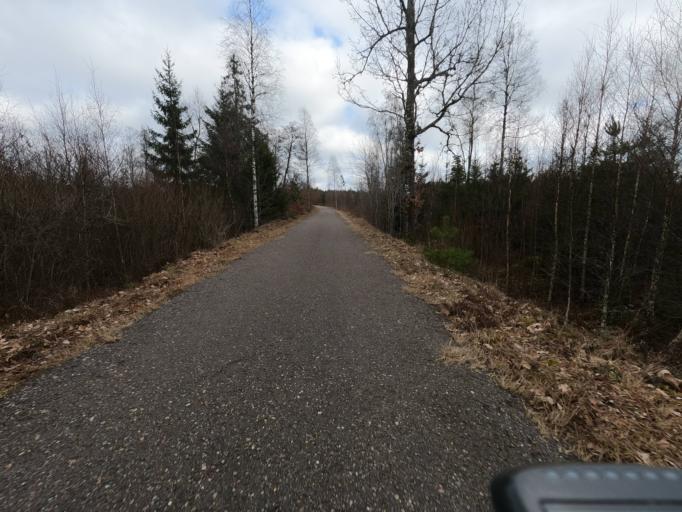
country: SE
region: Joenkoeping
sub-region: Varnamo Kommun
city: Rydaholm
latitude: 56.8414
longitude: 14.2300
